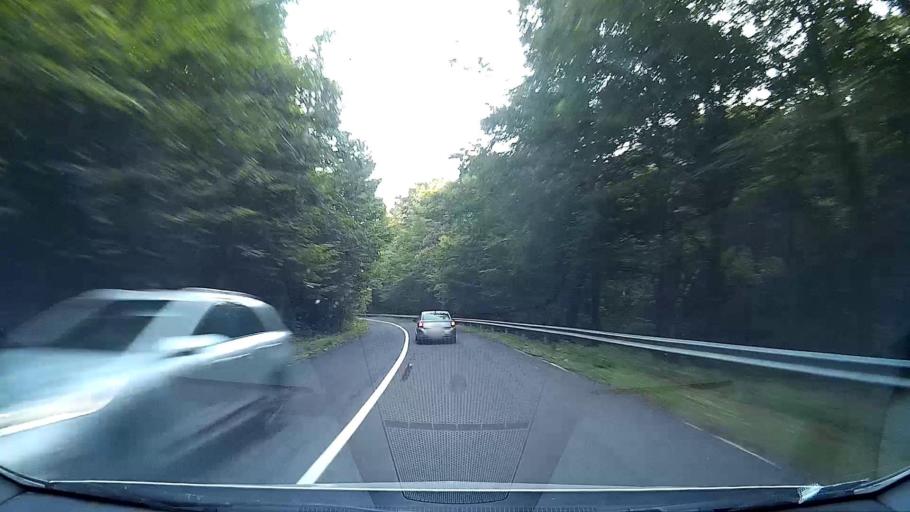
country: HU
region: Pest
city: Visegrad
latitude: 47.7451
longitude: 18.9441
